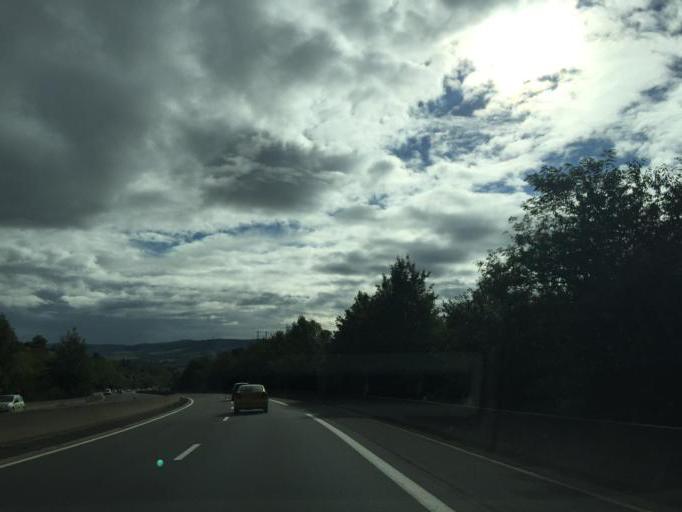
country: FR
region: Rhone-Alpes
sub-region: Departement de la Loire
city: La Grand-Croix
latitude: 45.4941
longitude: 4.5358
